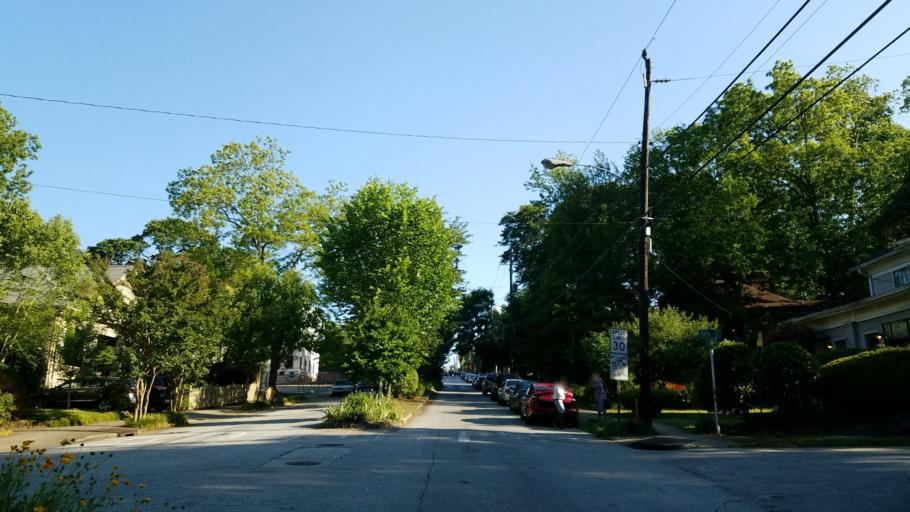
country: US
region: Georgia
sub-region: Fulton County
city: Atlanta
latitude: 33.7755
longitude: -84.3728
